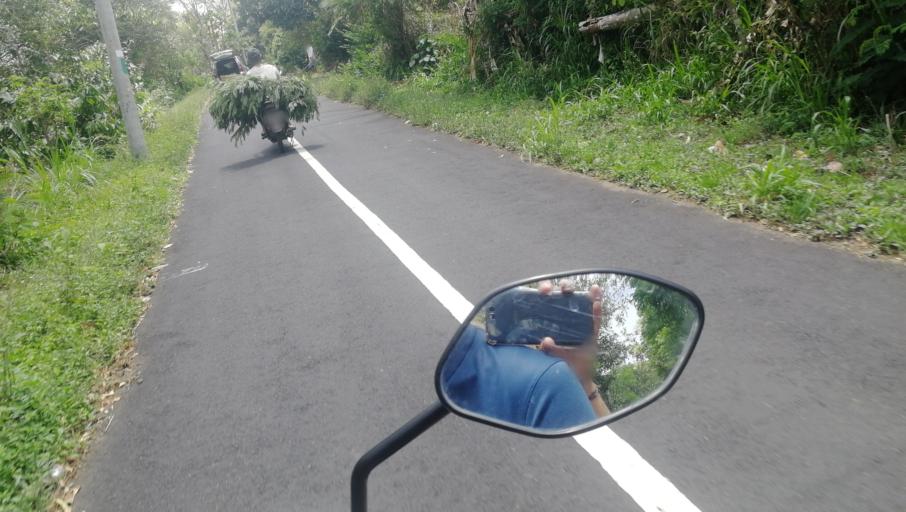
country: ID
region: Bali
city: Munduk
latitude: -8.2981
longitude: 115.0526
